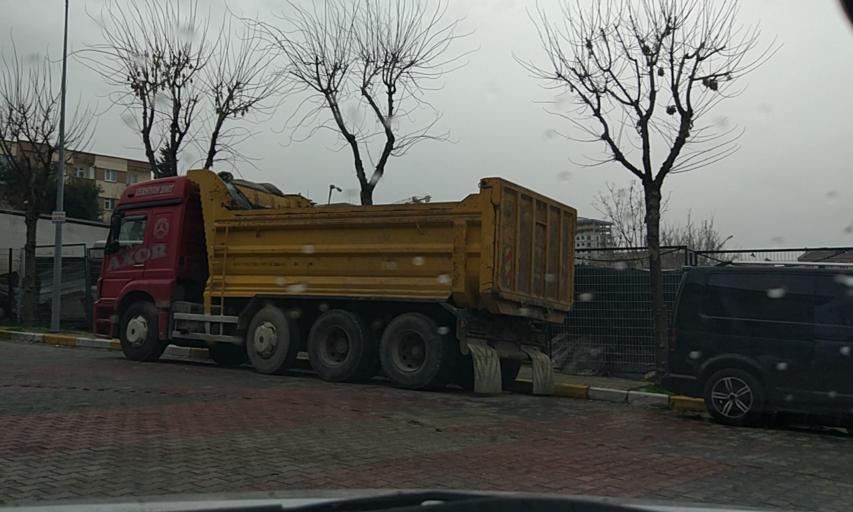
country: TR
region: Istanbul
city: Bagcilar
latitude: 41.0213
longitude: 28.8324
